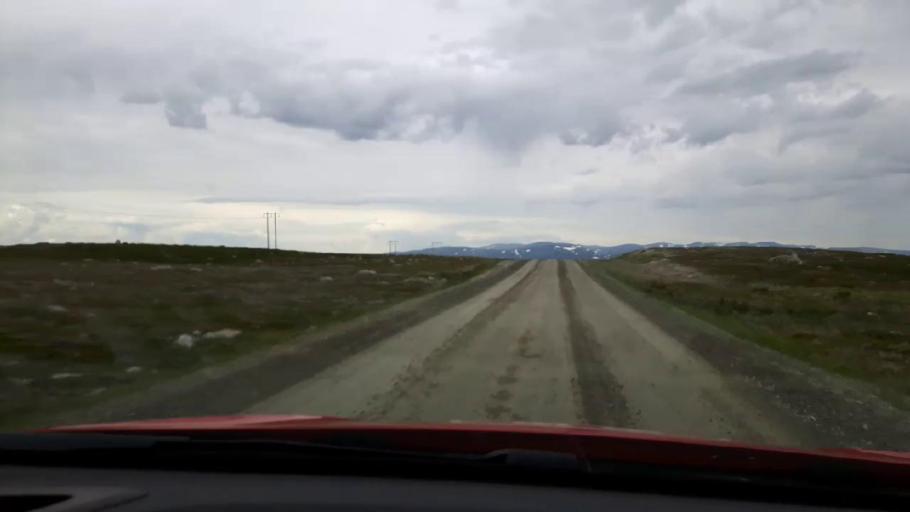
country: SE
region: Jaemtland
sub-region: Are Kommun
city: Are
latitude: 62.7496
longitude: 12.7484
